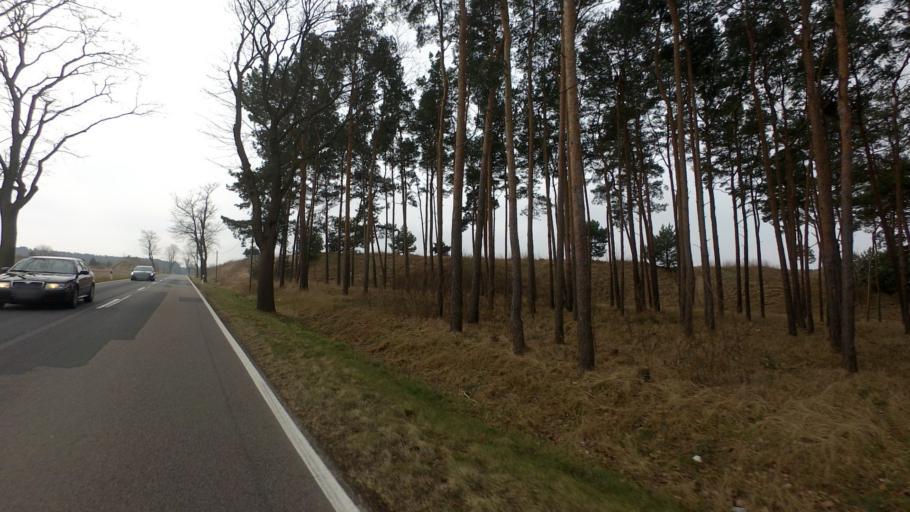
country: DE
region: Brandenburg
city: Linthe
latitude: 52.1495
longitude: 12.7877
